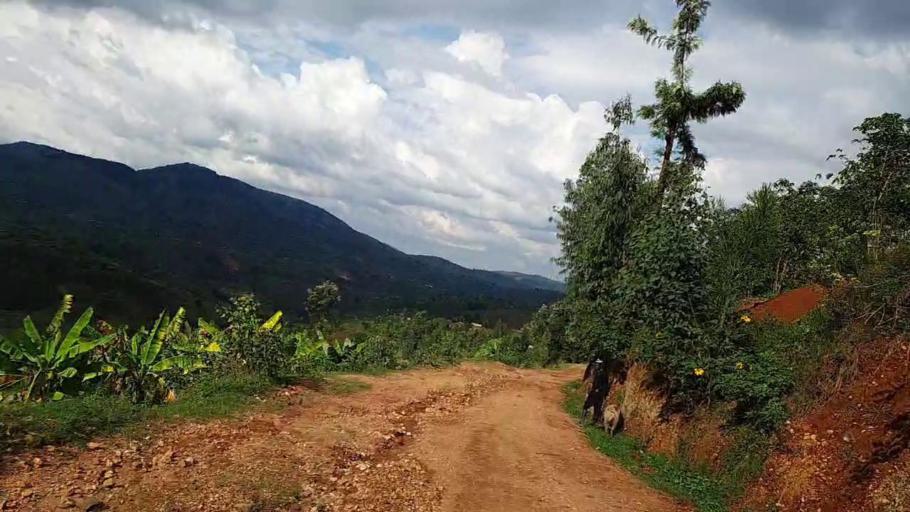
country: RW
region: Southern Province
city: Gikongoro
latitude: -2.4258
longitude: 29.6408
